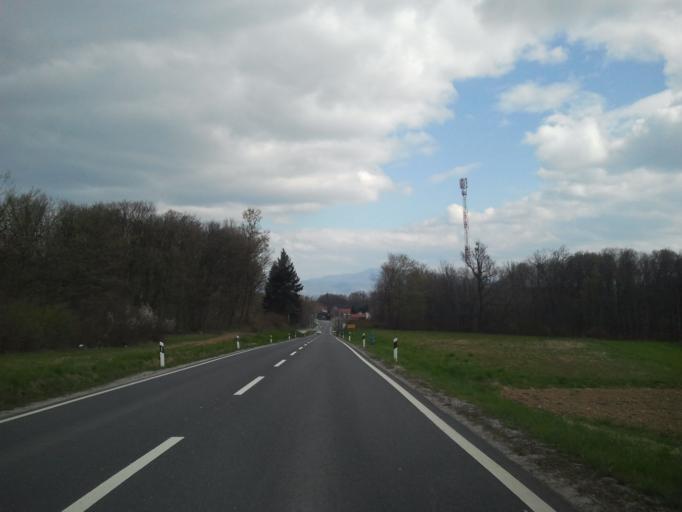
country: HR
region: Zagrebacka
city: Kerestinec
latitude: 45.7289
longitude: 15.7856
